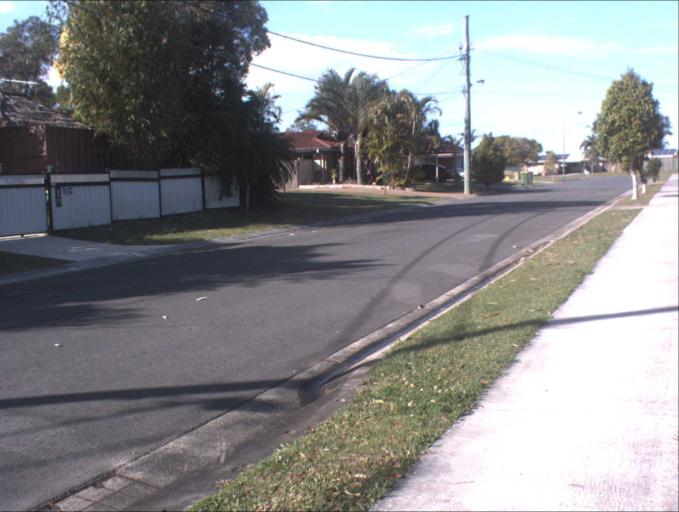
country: AU
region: Queensland
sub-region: Logan
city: Logan City
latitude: -27.6679
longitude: 153.1010
